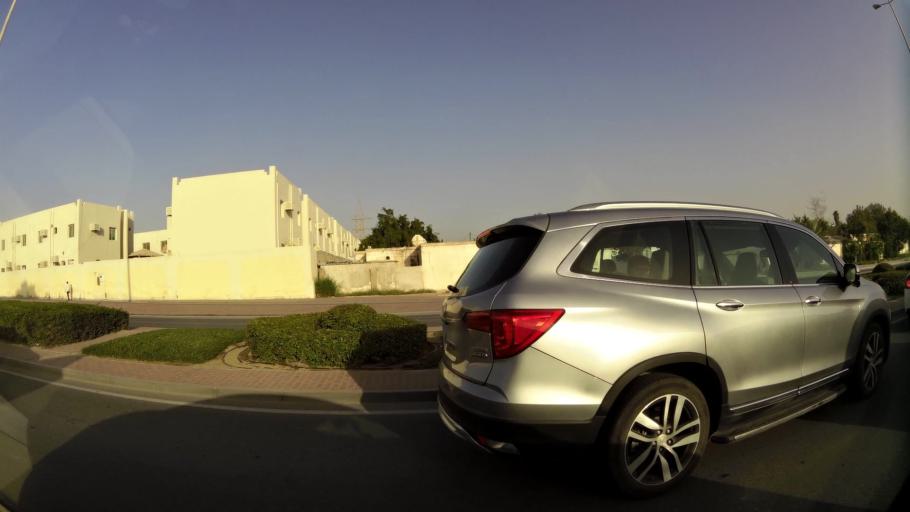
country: QA
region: Baladiyat ar Rayyan
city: Ar Rayyan
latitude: 25.3288
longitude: 51.4614
